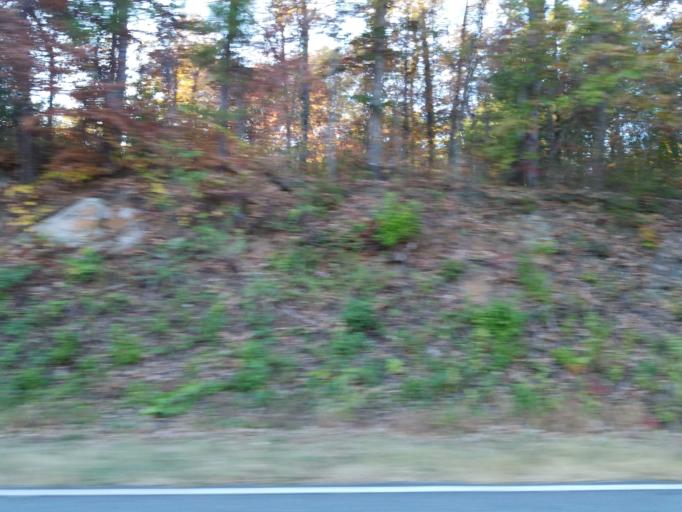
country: US
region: Georgia
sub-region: Gilmer County
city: Ellijay
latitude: 34.6137
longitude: -84.3937
